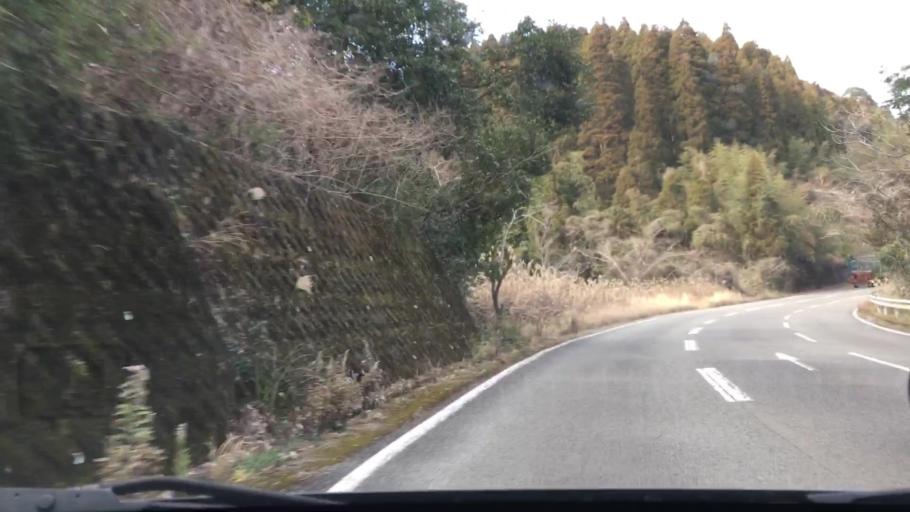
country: JP
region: Miyazaki
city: Nichinan
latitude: 31.6310
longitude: 131.3388
